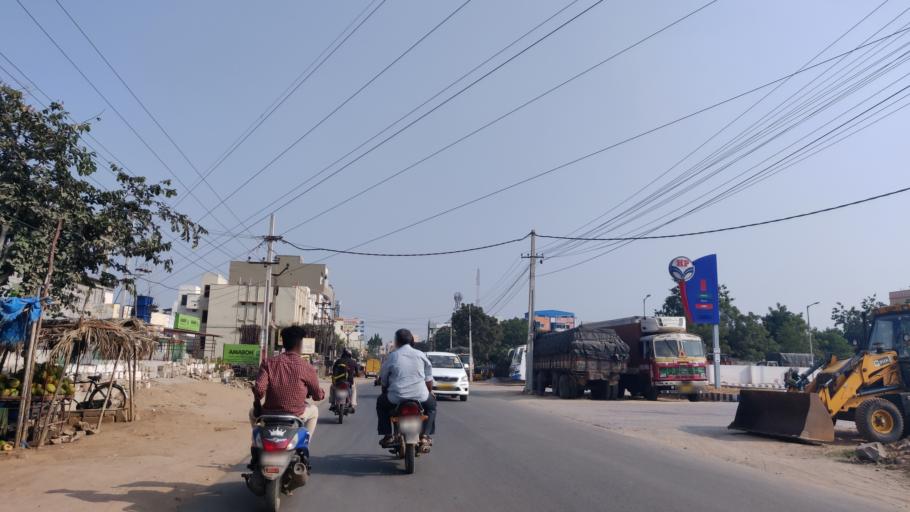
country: IN
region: Telangana
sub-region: Rangareddi
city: Uppal Kalan
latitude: 17.3968
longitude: 78.5895
